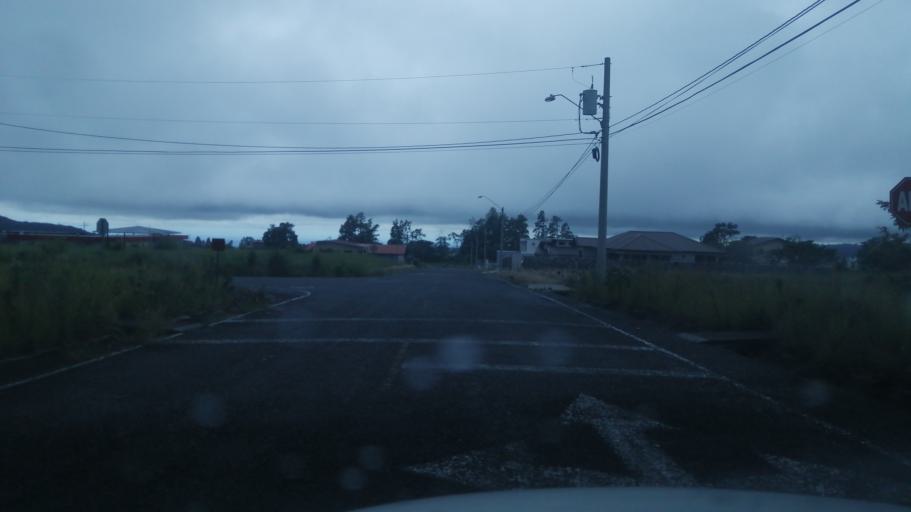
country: PA
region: Chiriqui
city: Palmira
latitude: 8.7180
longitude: -82.4417
